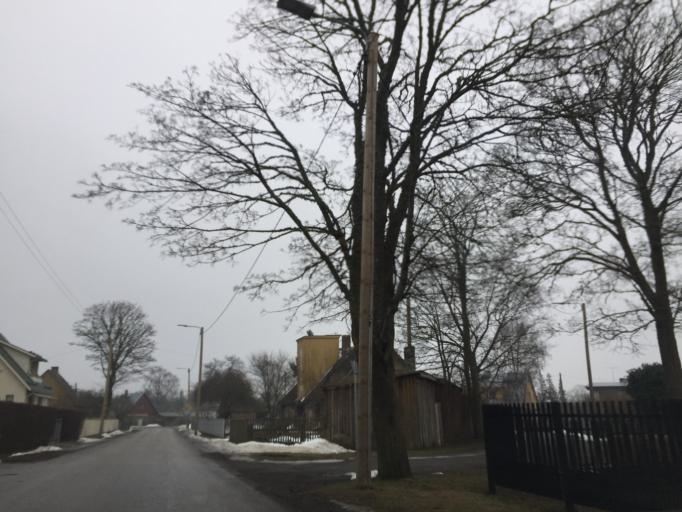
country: EE
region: Saare
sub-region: Kuressaare linn
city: Kuressaare
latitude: 58.2480
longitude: 22.4882
